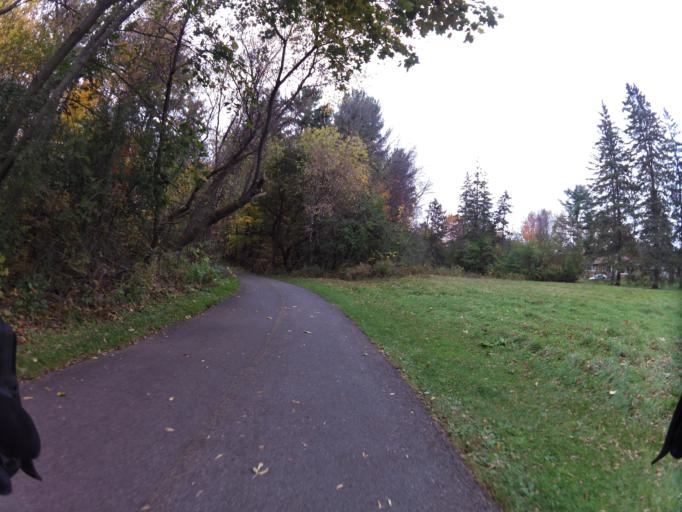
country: CA
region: Ontario
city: Ottawa
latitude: 45.4248
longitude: -75.7452
